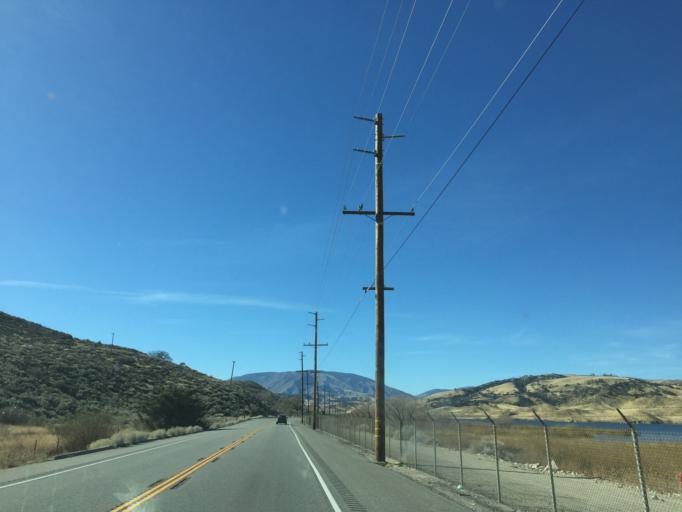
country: US
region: California
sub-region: Kern County
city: Lebec
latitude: 34.7685
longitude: -118.7417
